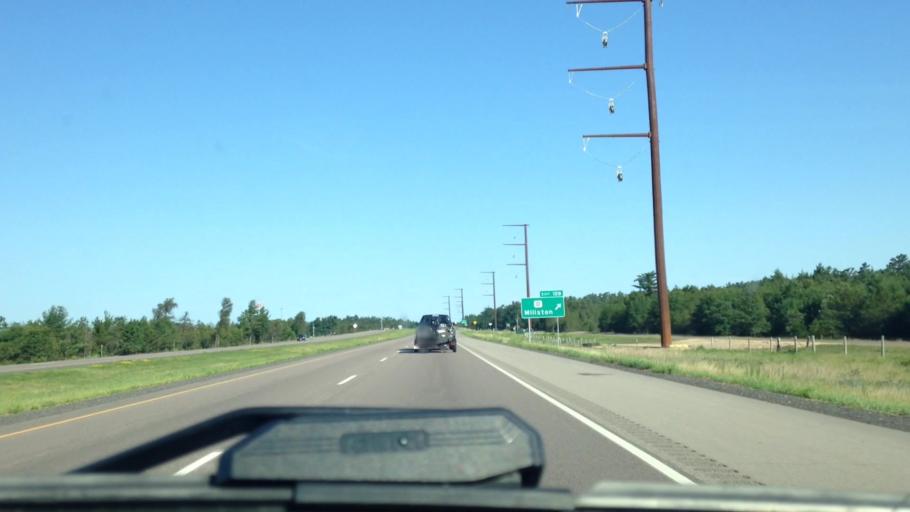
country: US
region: Wisconsin
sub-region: Jackson County
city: Black River Falls
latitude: 44.1900
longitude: -90.6326
